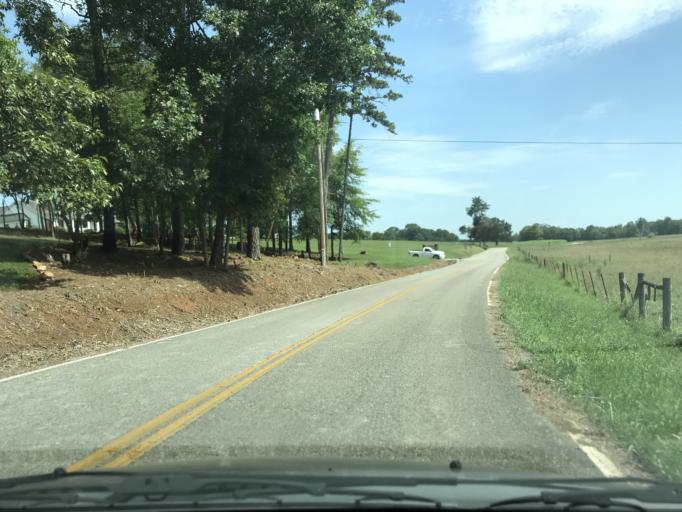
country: US
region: Tennessee
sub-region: Hamilton County
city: Lakesite
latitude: 35.2192
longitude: -85.0178
